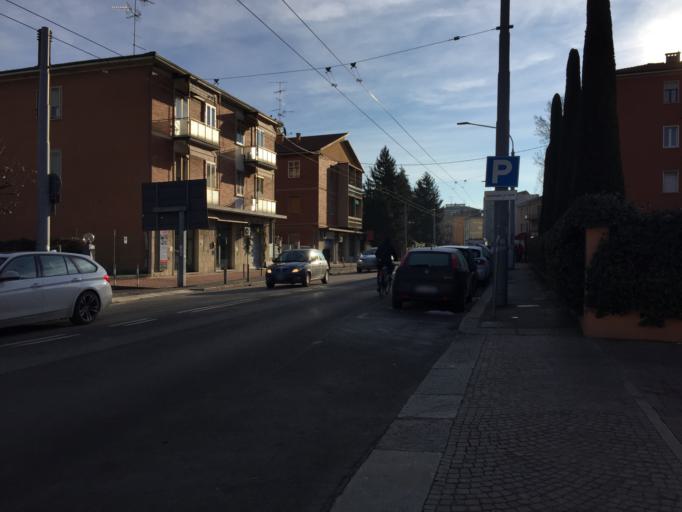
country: IT
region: Emilia-Romagna
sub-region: Provincia di Bologna
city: Casalecchio di Reno
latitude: 44.4942
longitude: 11.2960
